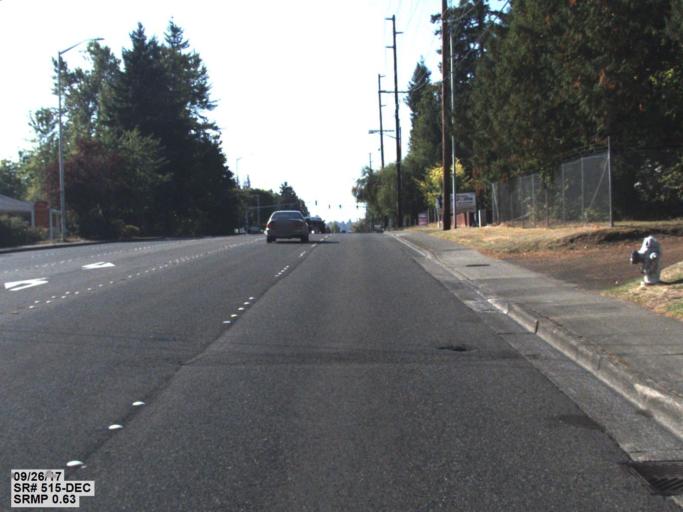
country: US
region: Washington
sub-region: King County
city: Kent
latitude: 47.3816
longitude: -122.2023
